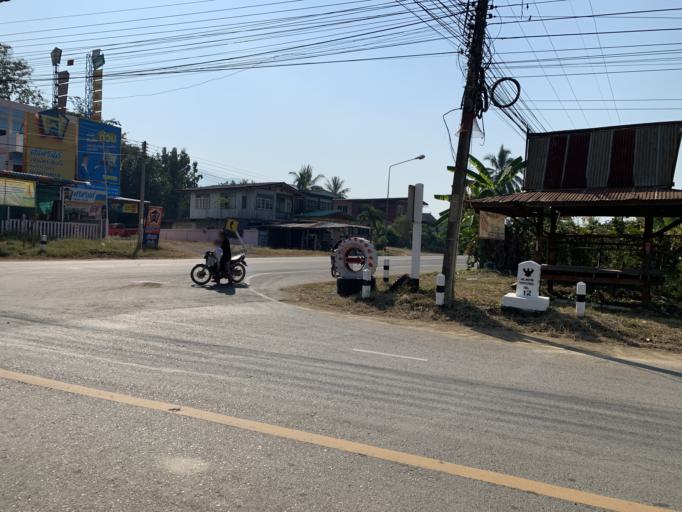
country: TH
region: Phetchabun
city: Phetchabun
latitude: 16.5466
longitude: 101.3184
